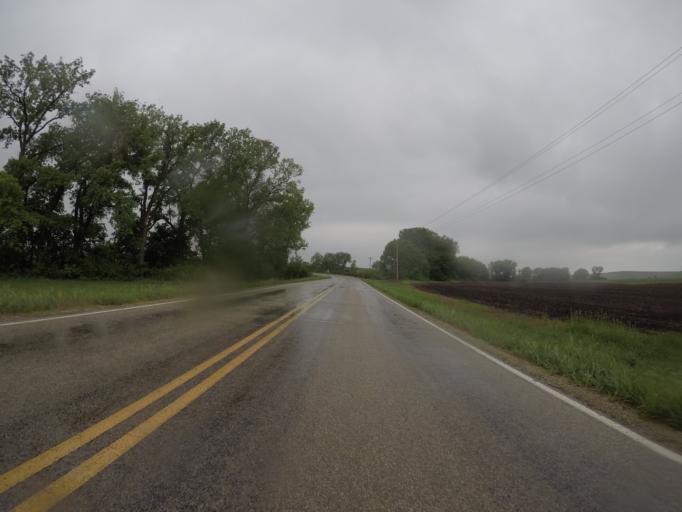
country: US
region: Kansas
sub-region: Pottawatomie County
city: Wamego
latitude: 39.3839
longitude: -96.2044
